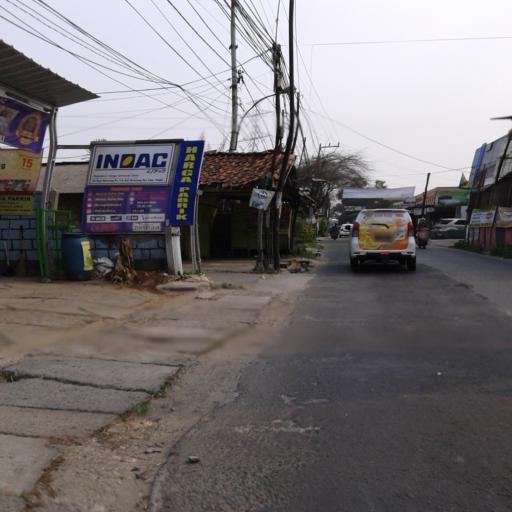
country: ID
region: West Java
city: Sawangan
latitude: -6.3720
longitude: 106.7729
